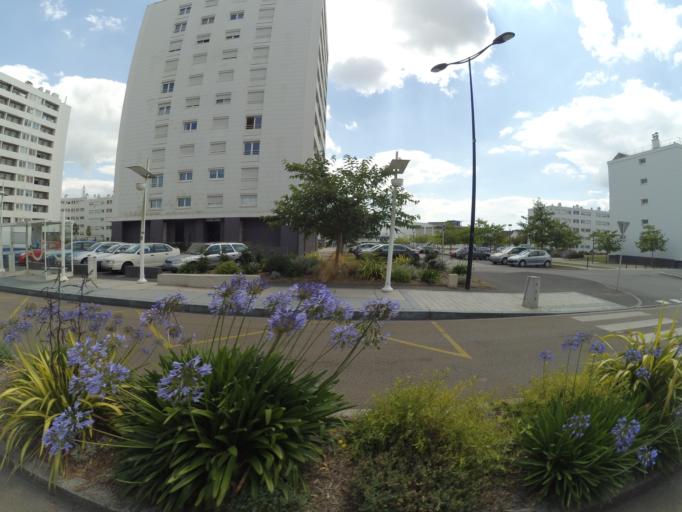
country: FR
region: Brittany
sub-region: Departement du Morbihan
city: Lanester
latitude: 47.7676
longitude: -3.3411
